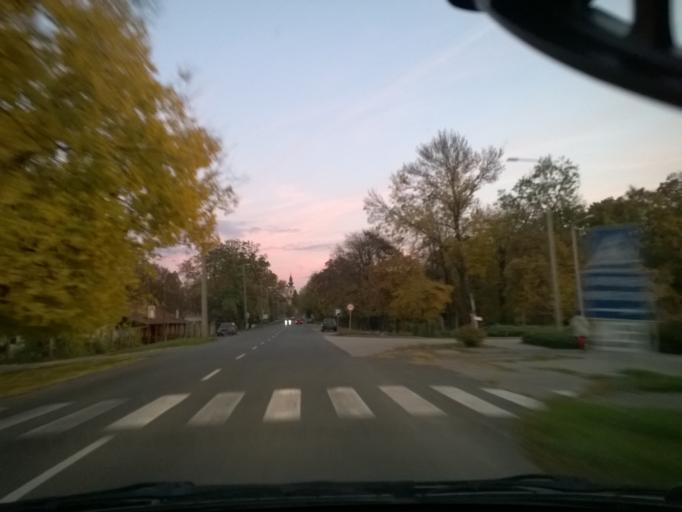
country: HU
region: Csongrad
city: Szentes
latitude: 46.6541
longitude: 20.2507
